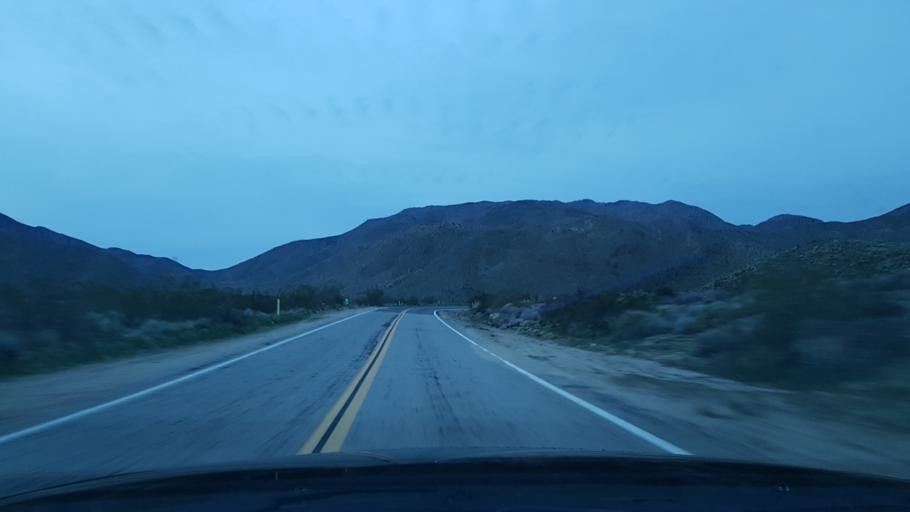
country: US
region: California
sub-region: San Diego County
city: Julian
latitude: 33.0039
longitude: -116.4543
